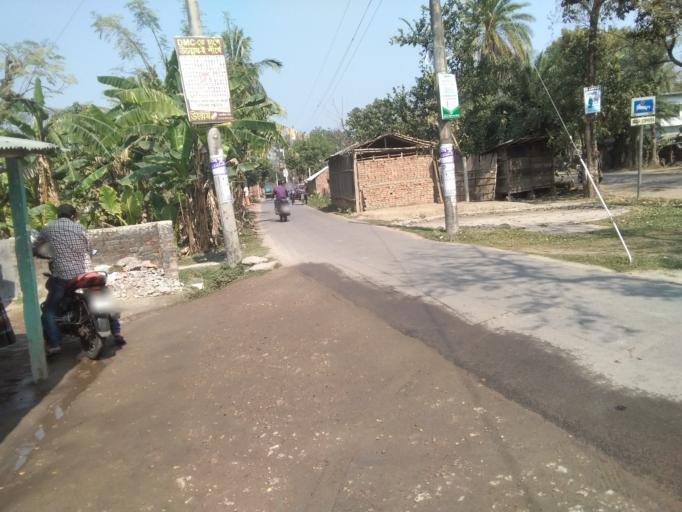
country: IN
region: West Bengal
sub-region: North 24 Parganas
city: Taki
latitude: 22.5904
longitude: 88.9998
